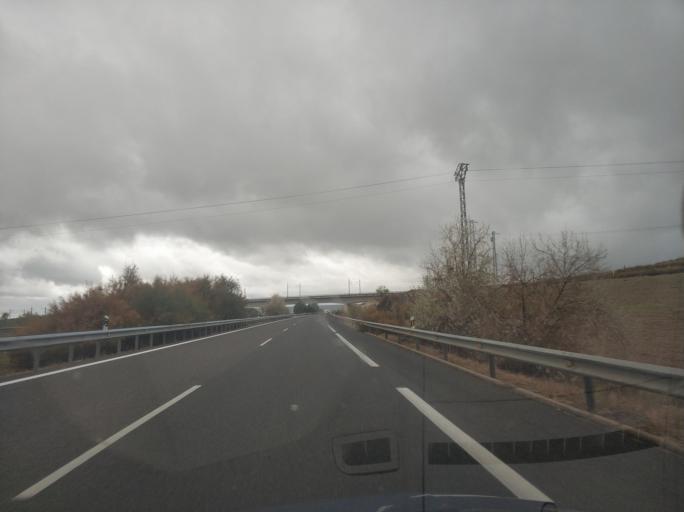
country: ES
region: Castille and Leon
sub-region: Provincia de Palencia
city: Soto de Cerrato
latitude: 41.9497
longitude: -4.4671
